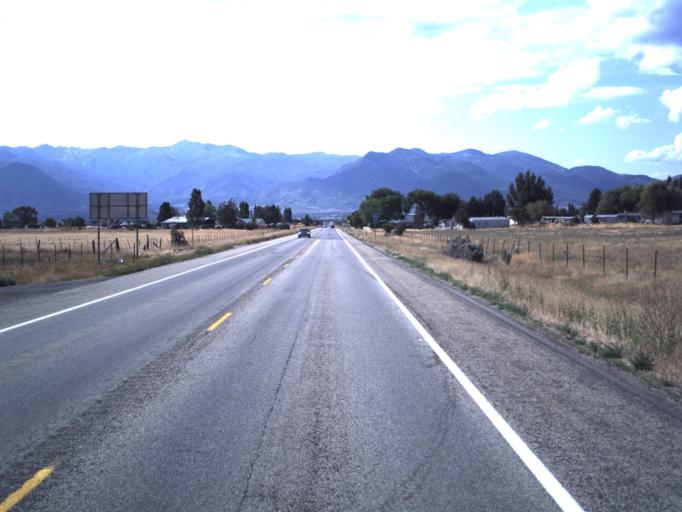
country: US
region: Utah
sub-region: Wasatch County
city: Heber
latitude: 40.4686
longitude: -111.3884
